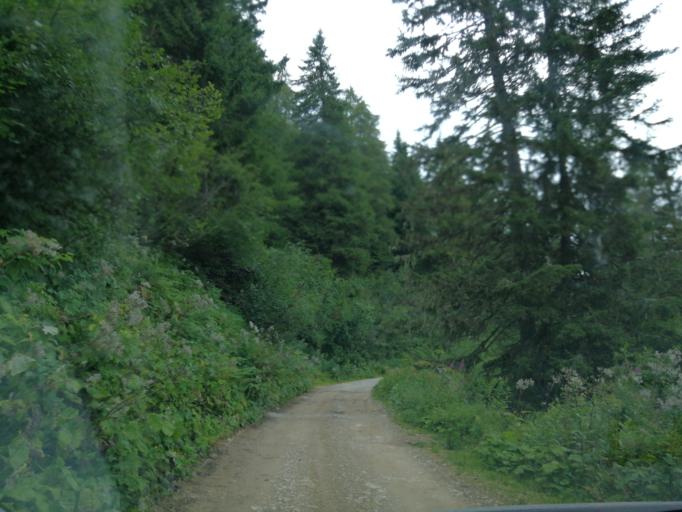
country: IT
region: Trentino-Alto Adige
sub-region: Provincia di Trento
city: Castel Condino
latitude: 45.9394
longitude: 10.5772
